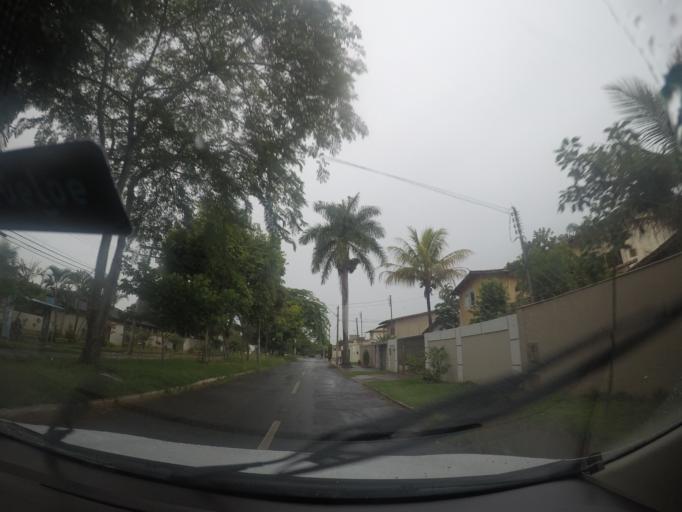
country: BR
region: Goias
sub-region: Goiania
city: Goiania
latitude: -16.6500
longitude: -49.2260
